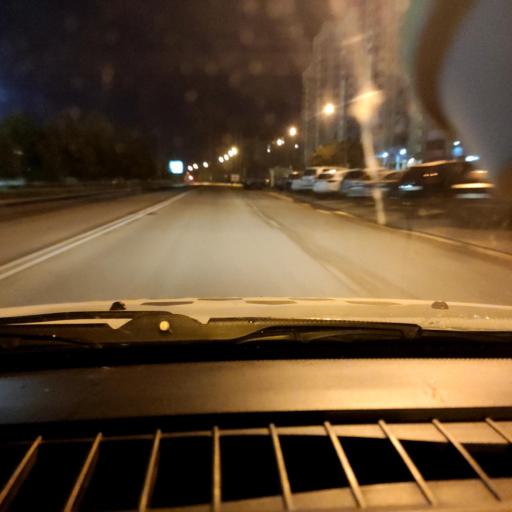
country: RU
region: Sverdlovsk
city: Yekaterinburg
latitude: 56.7959
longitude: 60.6222
